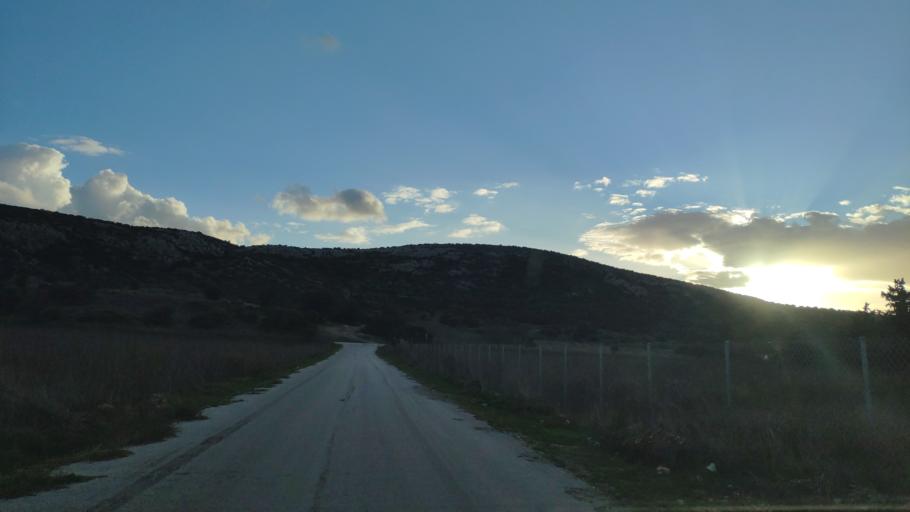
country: GR
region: Attica
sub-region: Nomarchia Anatolikis Attikis
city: Limin Mesoyaias
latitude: 37.9235
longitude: 23.9975
